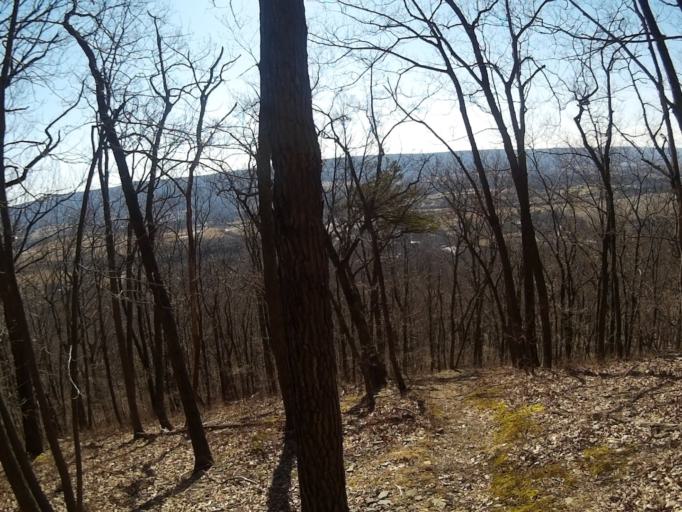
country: US
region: Pennsylvania
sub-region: Centre County
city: Lemont
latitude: 40.8061
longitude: -77.7982
